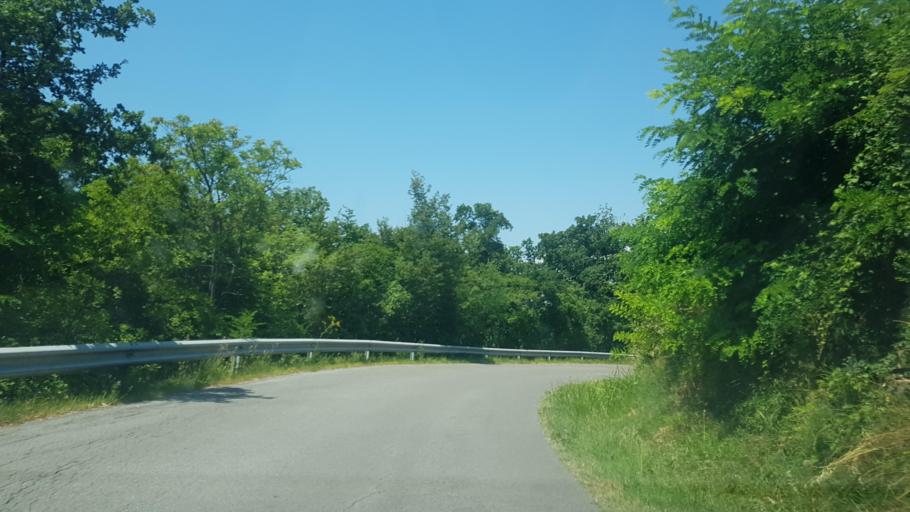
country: SI
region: Koper-Capodistria
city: Spodnje Skofije
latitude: 45.5839
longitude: 13.7769
